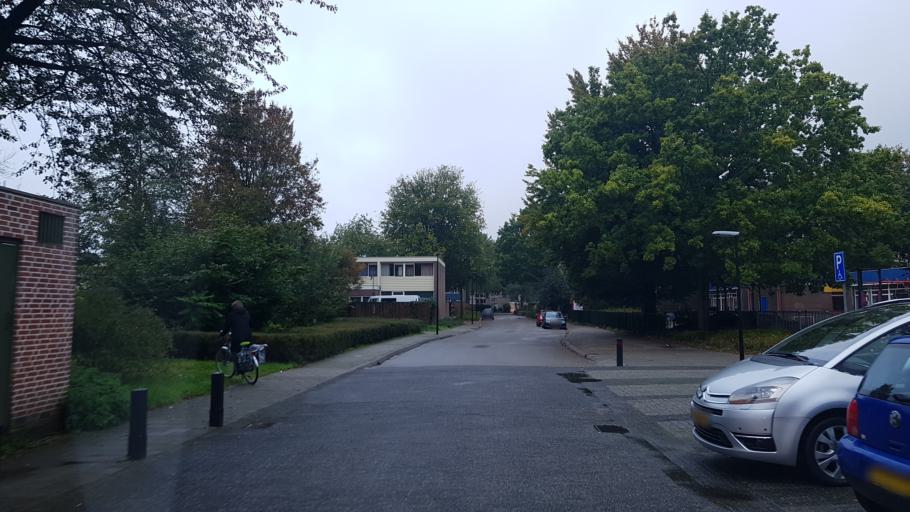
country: NL
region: Gelderland
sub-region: Gemeente Apeldoorn
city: Apeldoorn
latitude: 52.2037
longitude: 5.9946
